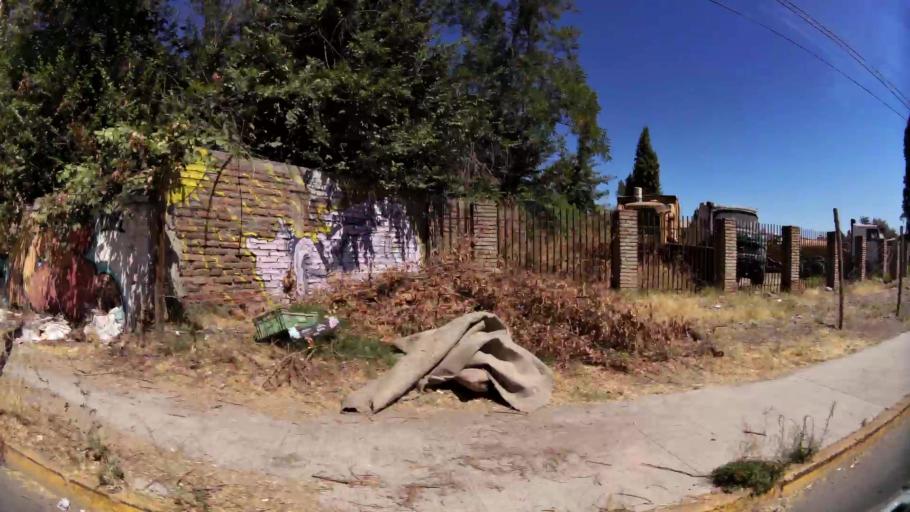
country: CL
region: O'Higgins
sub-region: Provincia de Cachapoal
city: Rancagua
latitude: -34.1651
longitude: -70.7706
